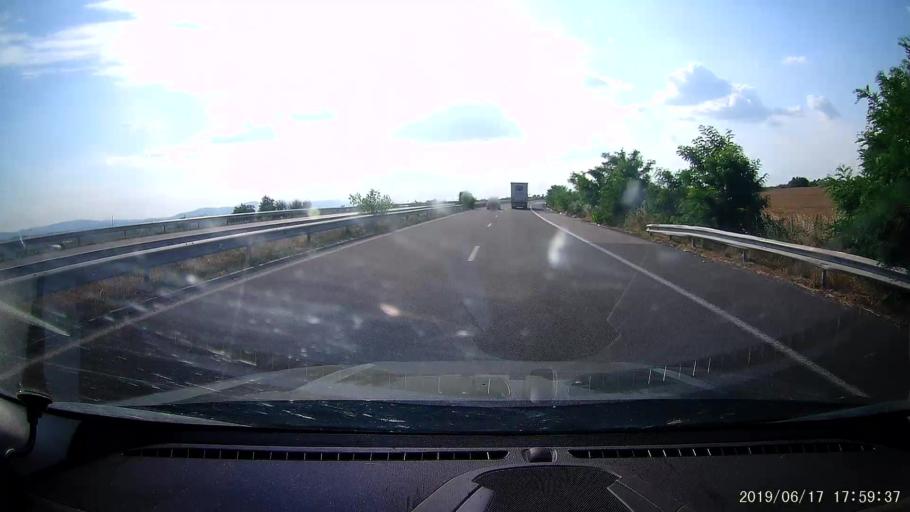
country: BG
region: Khaskovo
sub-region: Obshtina Svilengrad
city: Svilengrad
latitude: 41.7253
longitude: 26.2934
